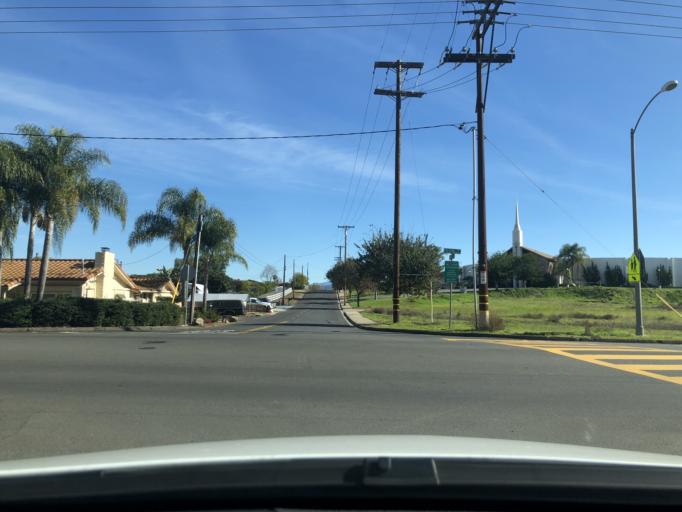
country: US
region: California
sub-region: San Diego County
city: Escondido
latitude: 33.0964
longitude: -117.0835
